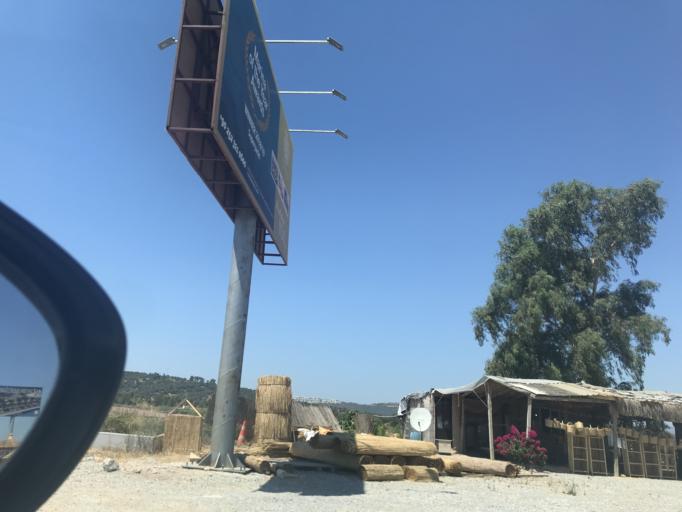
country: TR
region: Mugla
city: Kiulukioi
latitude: 37.1682
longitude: 27.5938
